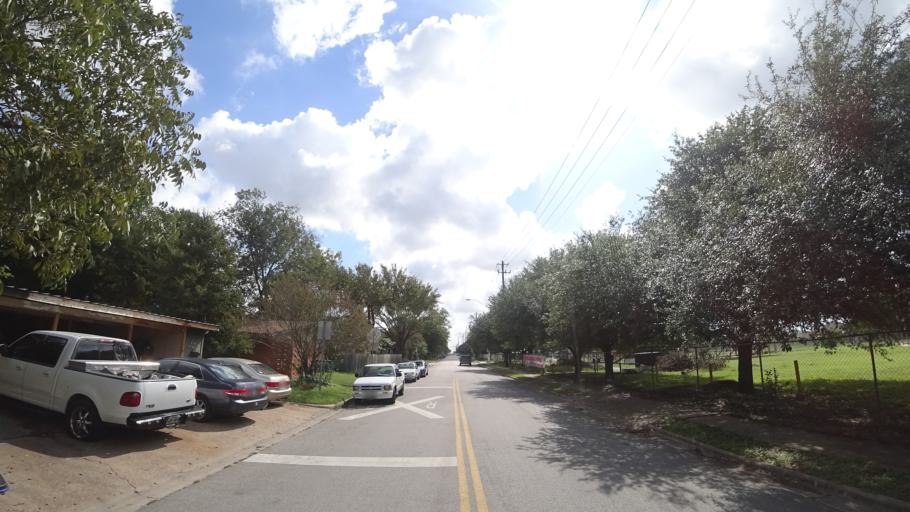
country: US
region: Texas
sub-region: Travis County
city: Austin
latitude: 30.3471
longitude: -97.7214
